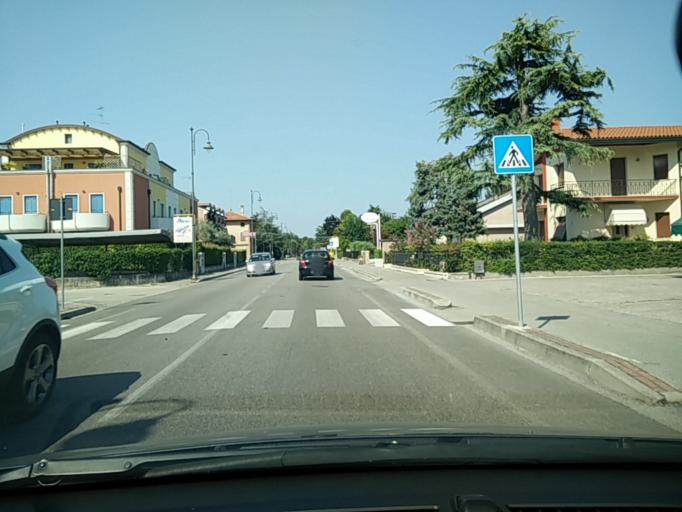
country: IT
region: Veneto
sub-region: Provincia di Venezia
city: San Giorgio di Livenza
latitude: 45.6483
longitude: 12.7947
